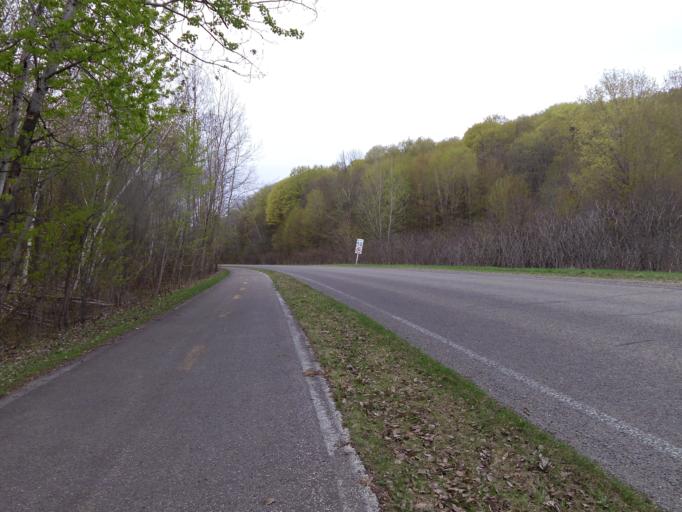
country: CA
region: Quebec
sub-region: Laurentides
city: Oka
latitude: 45.4820
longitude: -74.0393
